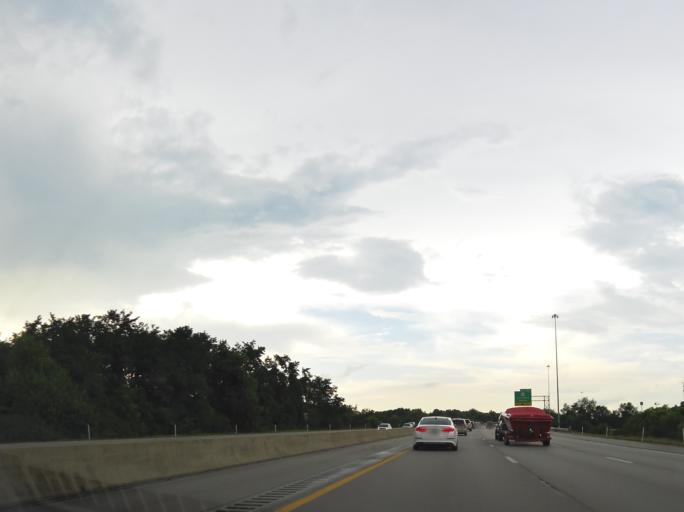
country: US
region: Kentucky
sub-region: Fayette County
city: Lexington
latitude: 37.9531
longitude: -84.3878
